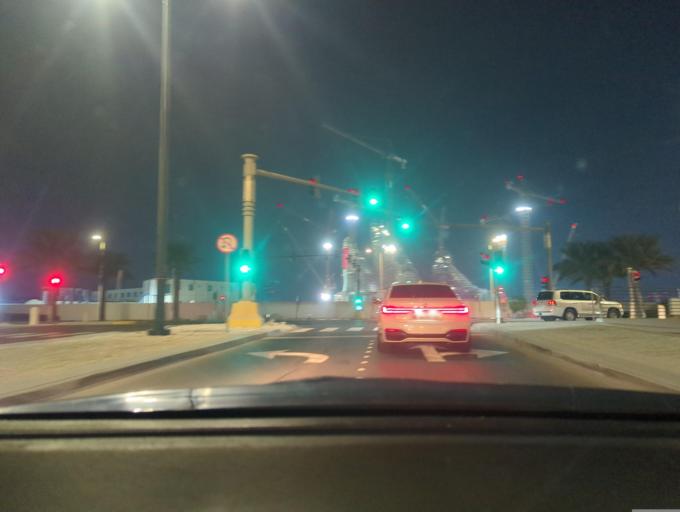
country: AE
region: Abu Dhabi
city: Abu Dhabi
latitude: 24.5380
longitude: 54.4089
